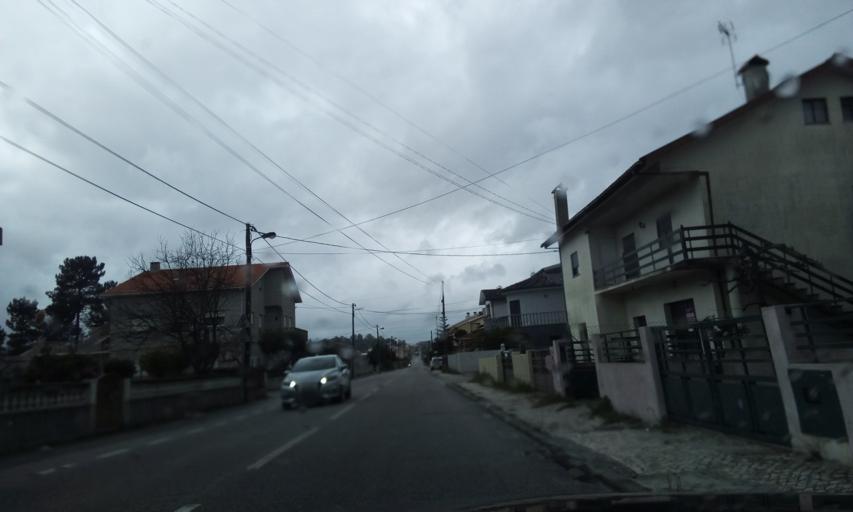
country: PT
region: Viseu
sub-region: Viseu
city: Rio de Loba
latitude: 40.6309
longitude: -7.8652
